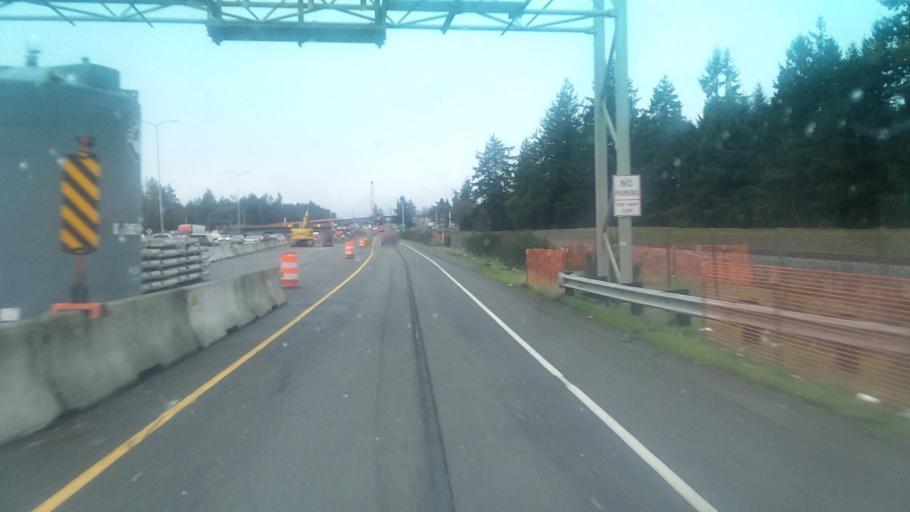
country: US
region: Washington
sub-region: Pierce County
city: Fort Lewis
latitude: 47.1297
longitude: -122.5387
